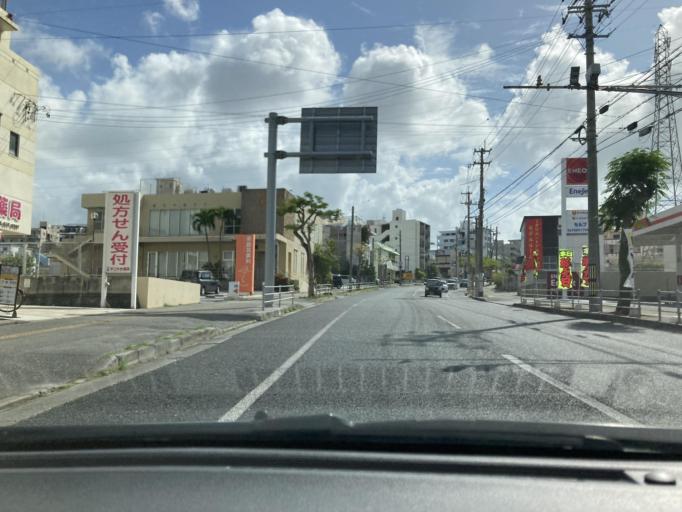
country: JP
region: Okinawa
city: Tomigusuku
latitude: 26.1914
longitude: 127.6753
